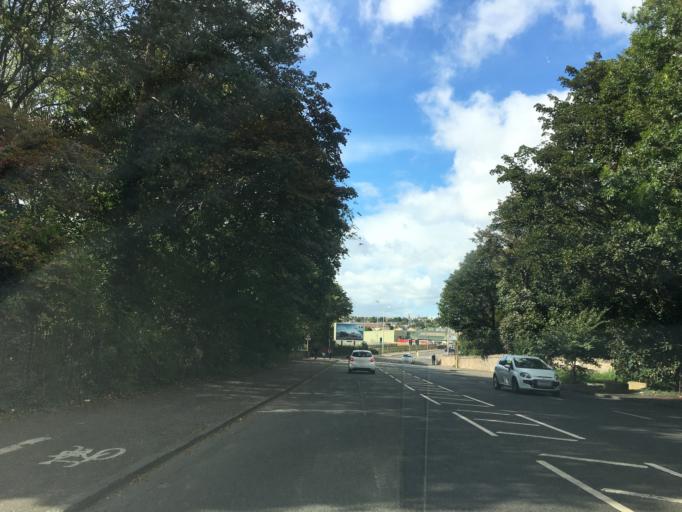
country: GB
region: Scotland
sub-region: West Lothian
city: Seafield
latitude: 55.9319
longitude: -3.1469
